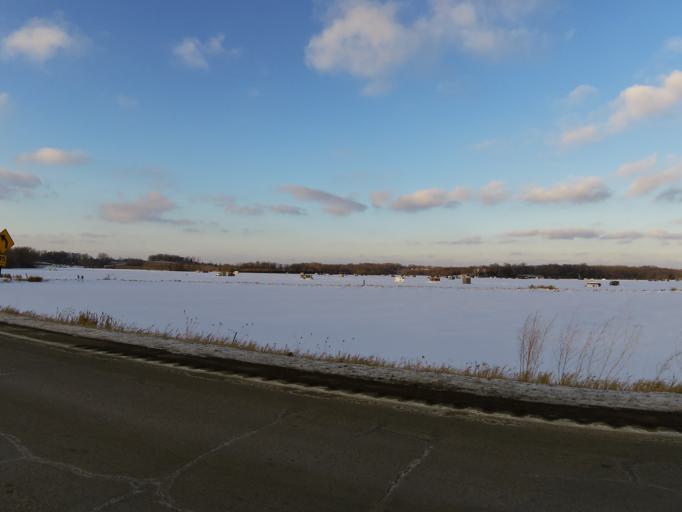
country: US
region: Minnesota
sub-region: Scott County
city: Prior Lake
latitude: 44.6289
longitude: -93.4169
